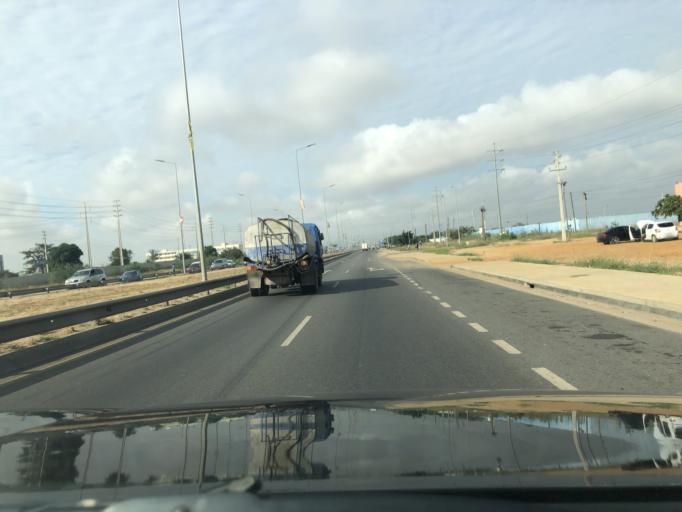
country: AO
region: Luanda
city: Luanda
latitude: -8.9622
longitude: 13.2564
